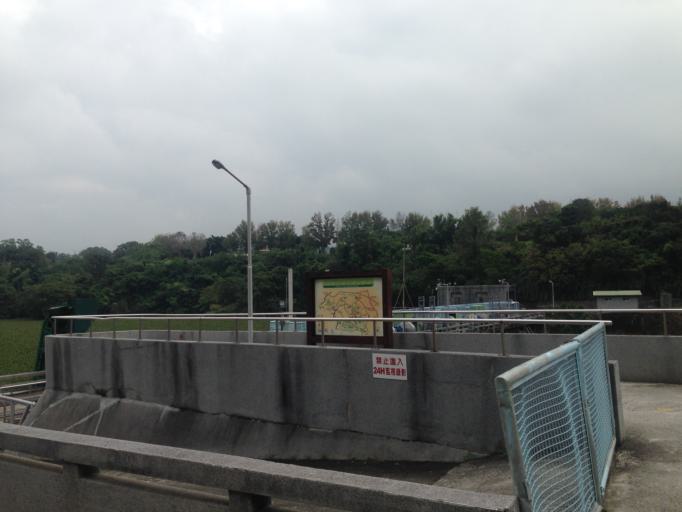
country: TW
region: Taiwan
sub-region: Hsinchu
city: Hsinchu
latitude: 24.6739
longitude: 120.9829
